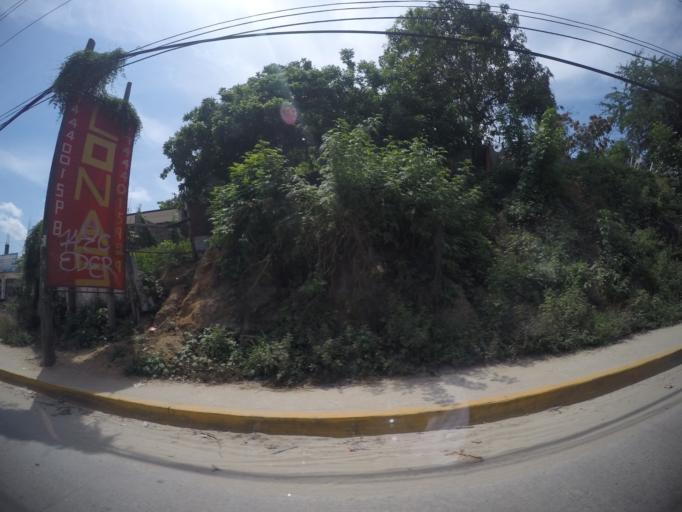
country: MX
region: Guerrero
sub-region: Acapulco de Juarez
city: Colonia Nueva Revolucion
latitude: 16.9158
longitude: -99.8214
